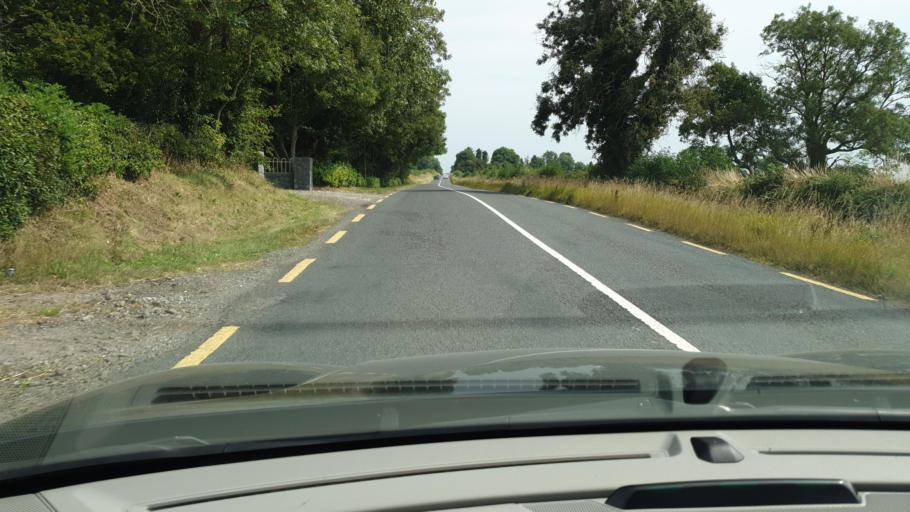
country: IE
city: Kentstown
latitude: 53.6344
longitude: -6.5833
